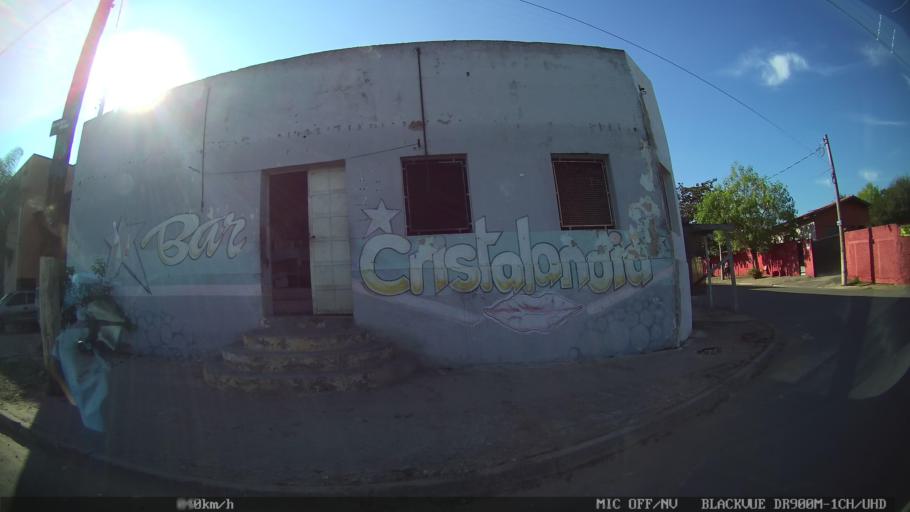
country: BR
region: Sao Paulo
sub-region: Campinas
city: Campinas
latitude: -22.9801
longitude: -47.1092
